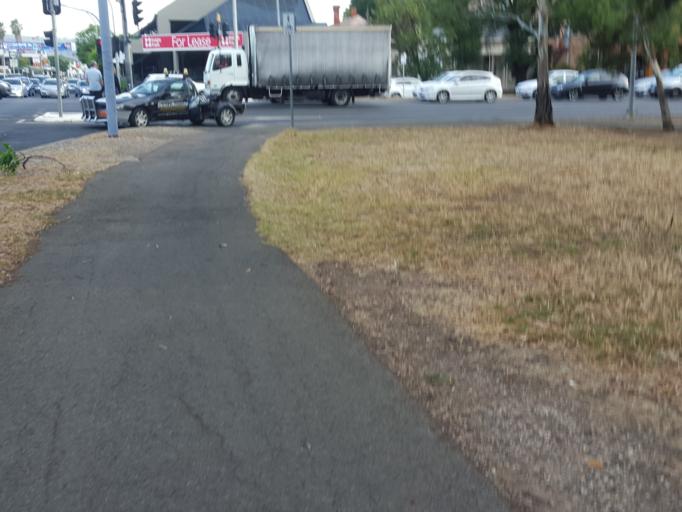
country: AU
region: South Australia
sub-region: Unley
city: Unley
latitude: -34.9405
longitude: 138.6066
